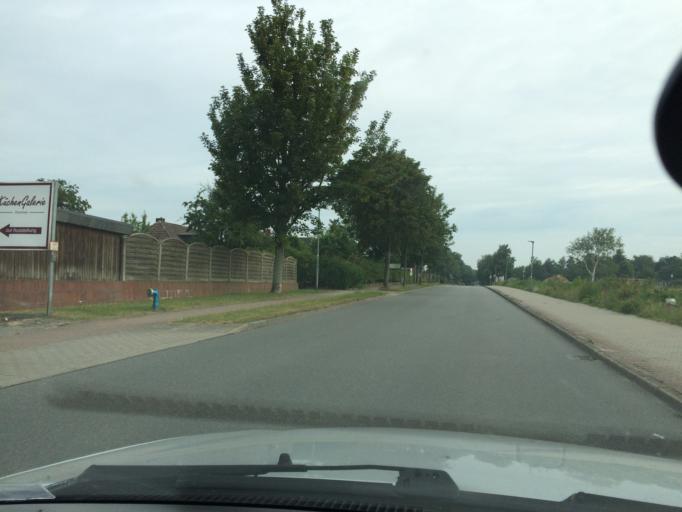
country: DE
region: Schleswig-Holstein
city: Oeversee
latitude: 54.6976
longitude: 9.4283
